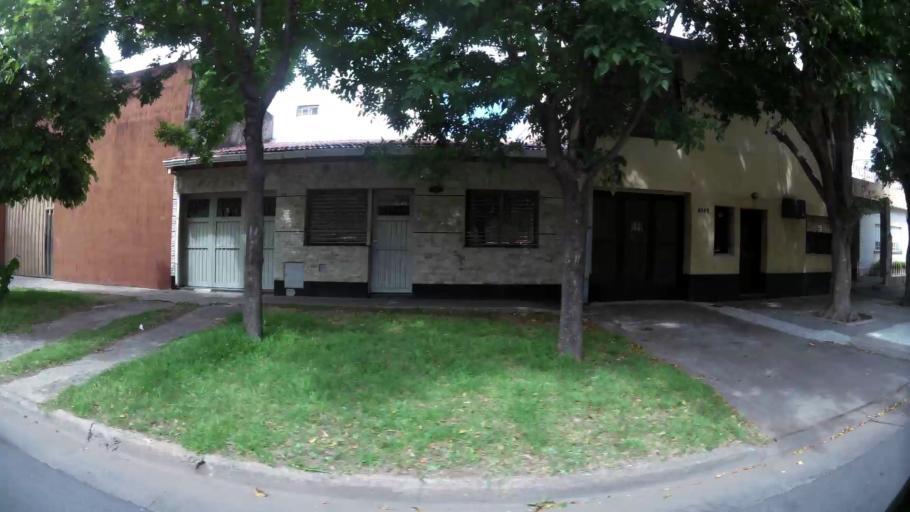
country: AR
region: Santa Fe
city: Gobernador Galvez
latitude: -32.9964
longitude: -60.6320
